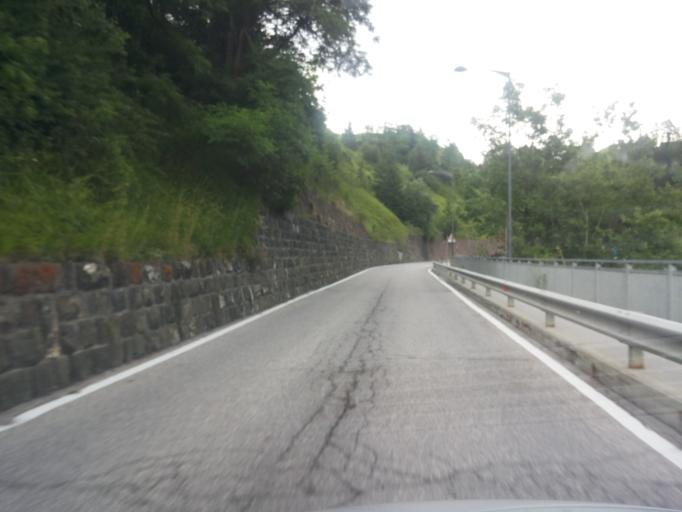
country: IT
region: Trentino-Alto Adige
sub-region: Bolzano
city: Santa Cristina Valgardena
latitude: 46.5579
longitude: 11.7292
